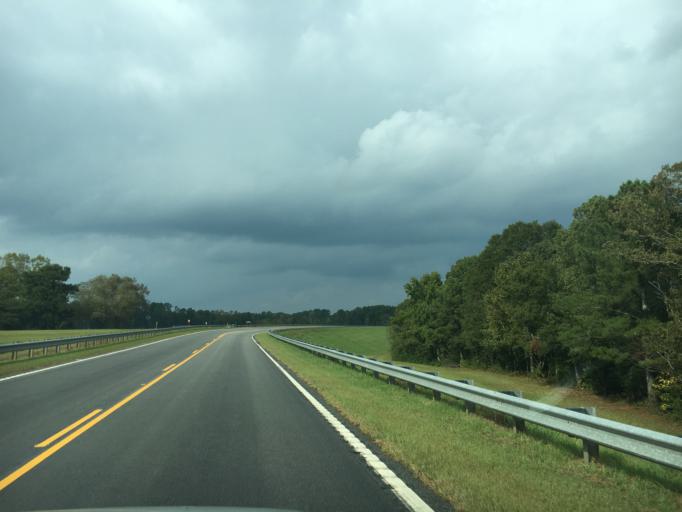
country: US
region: Georgia
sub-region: Hart County
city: Hartwell
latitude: 34.3662
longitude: -82.8148
